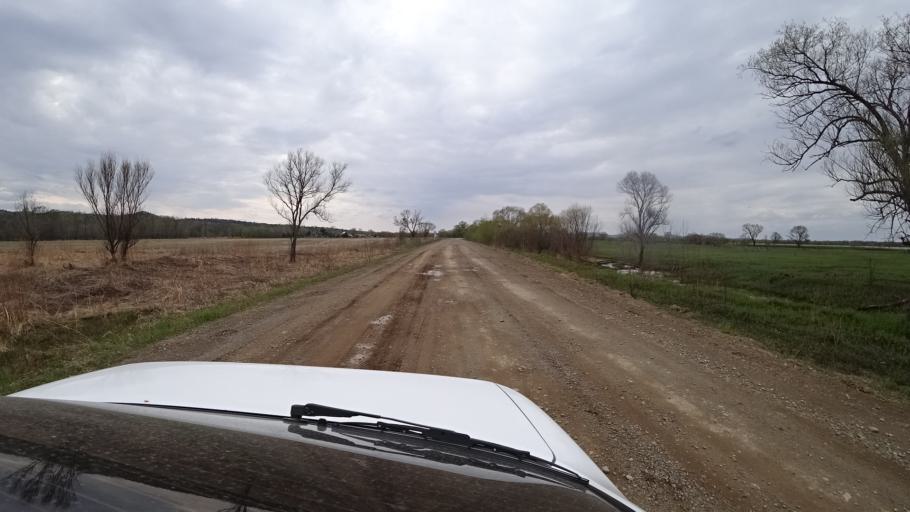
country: RU
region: Primorskiy
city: Novopokrovka
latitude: 45.4903
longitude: 134.4575
